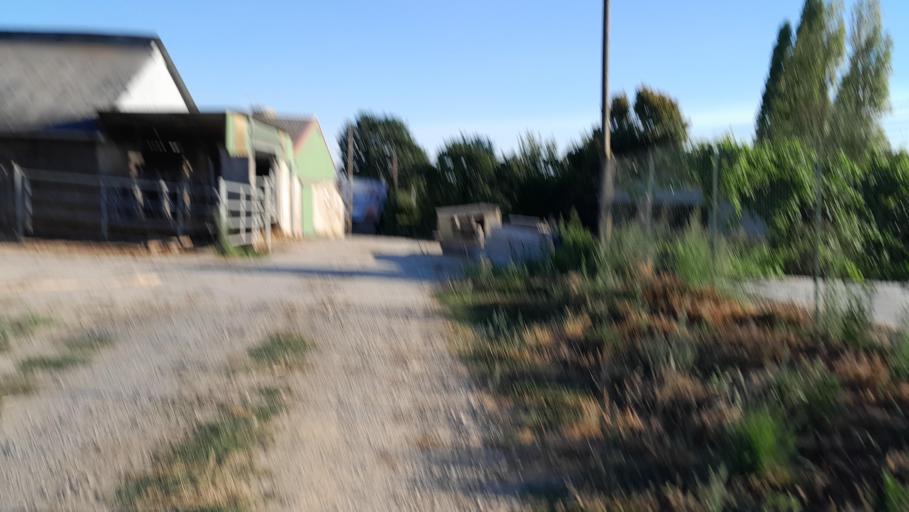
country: FR
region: Pays de la Loire
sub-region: Departement de la Mayenne
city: Ballots
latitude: 47.9605
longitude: -1.0609
